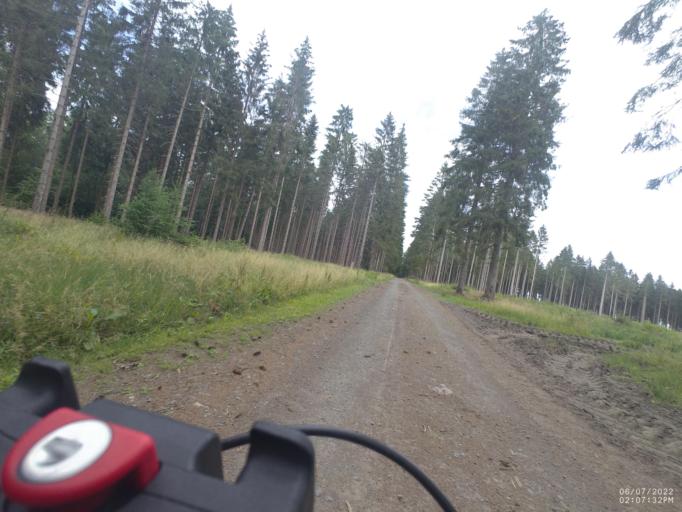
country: DE
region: Rheinland-Pfalz
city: Meisburg
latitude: 50.1371
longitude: 6.6612
